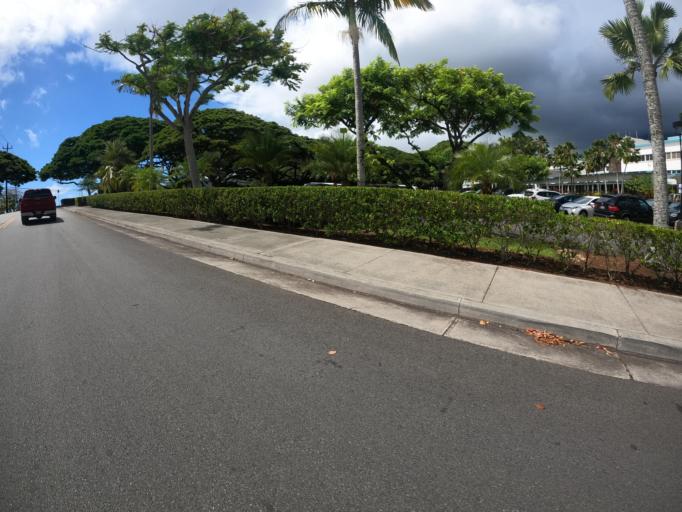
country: US
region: Hawaii
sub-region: Honolulu County
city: Maunawili
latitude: 21.3811
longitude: -157.7571
